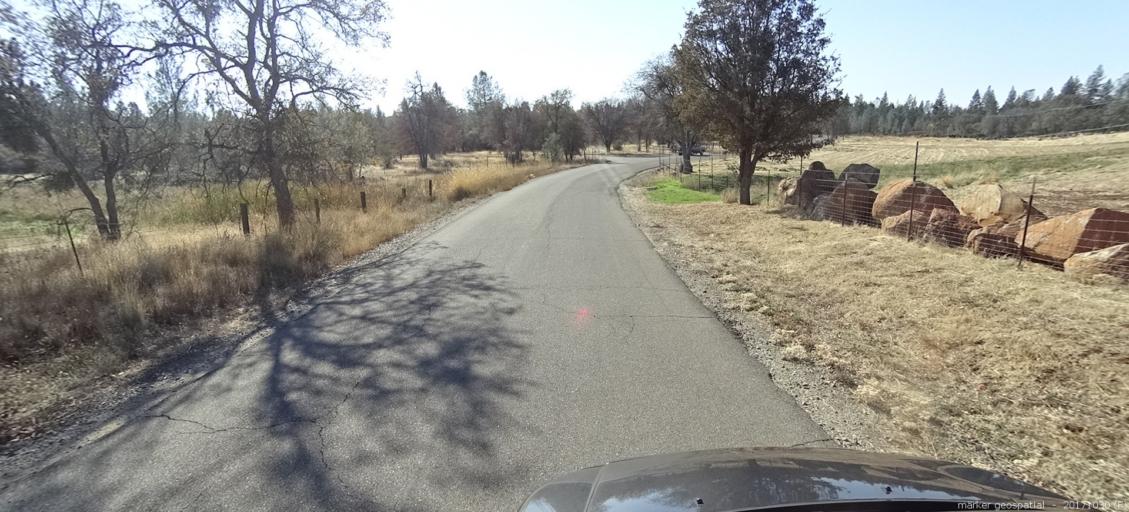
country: US
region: California
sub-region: Shasta County
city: Shingletown
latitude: 40.5092
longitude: -121.9949
